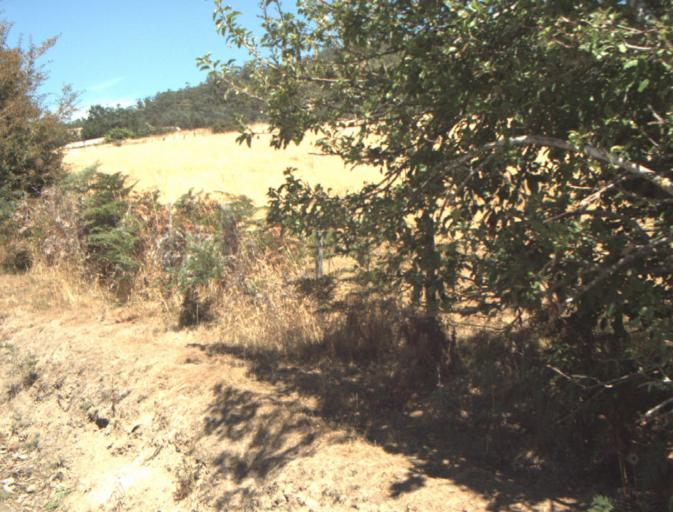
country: AU
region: Tasmania
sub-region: Launceston
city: Mayfield
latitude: -41.2463
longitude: 147.1214
